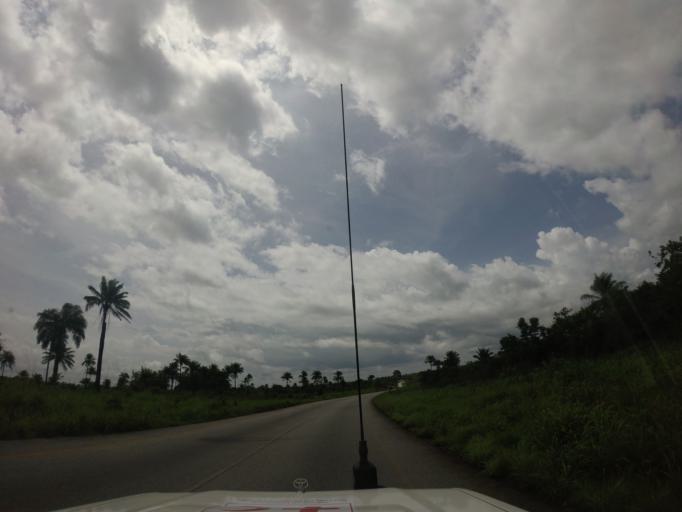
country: SL
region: Northern Province
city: Lunsar
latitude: 8.4822
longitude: -12.6450
